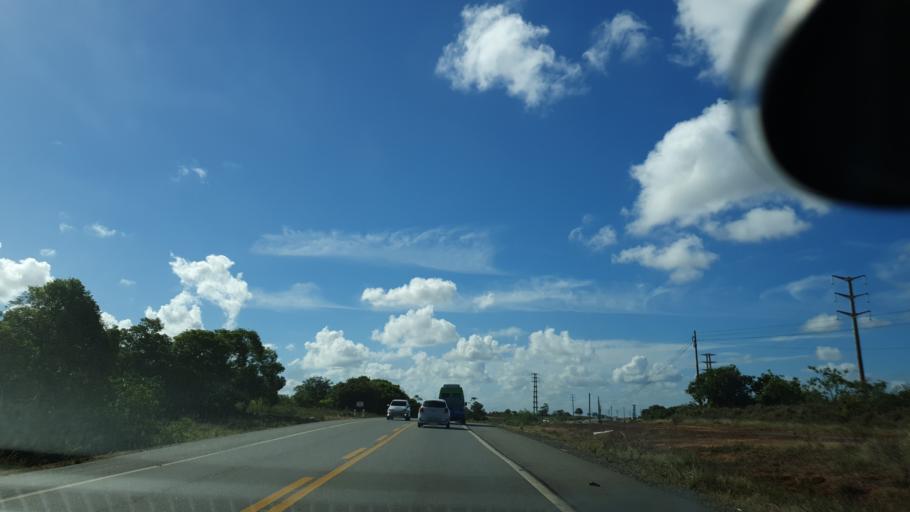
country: BR
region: Bahia
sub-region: Camacari
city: Camacari
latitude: -12.7027
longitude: -38.2137
